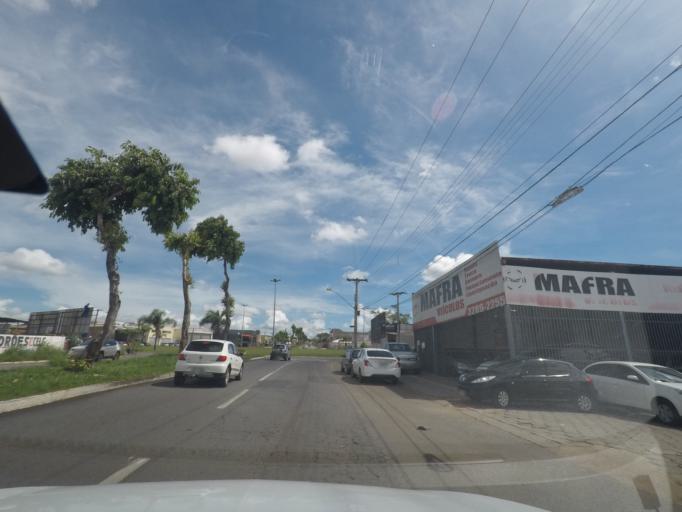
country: BR
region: Goias
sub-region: Goiania
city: Goiania
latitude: -16.7431
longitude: -49.3296
